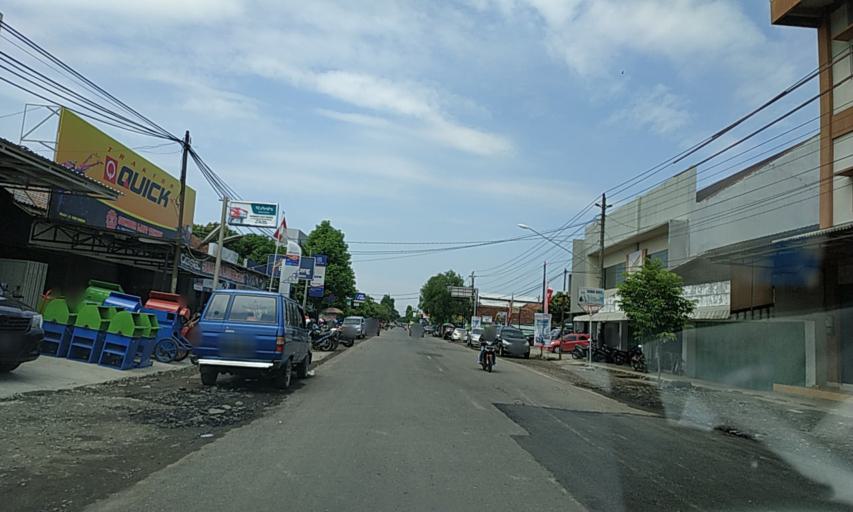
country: ID
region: Central Java
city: Sidareja
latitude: -7.4859
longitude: 108.7916
